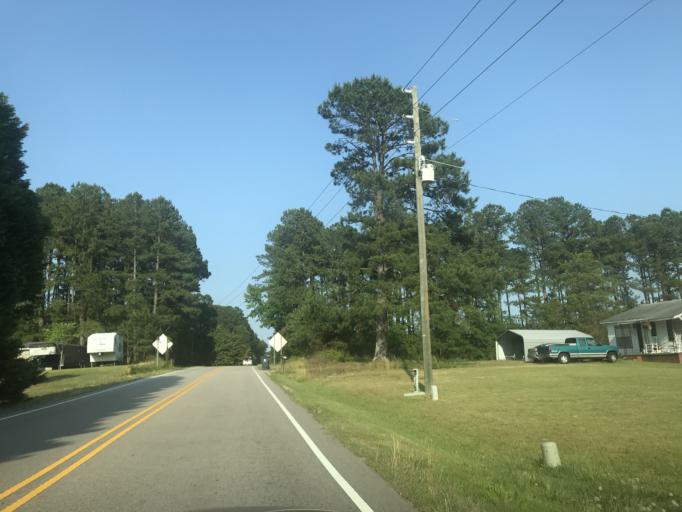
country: US
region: North Carolina
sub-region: Wake County
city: Rolesville
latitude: 35.8614
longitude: -78.4803
